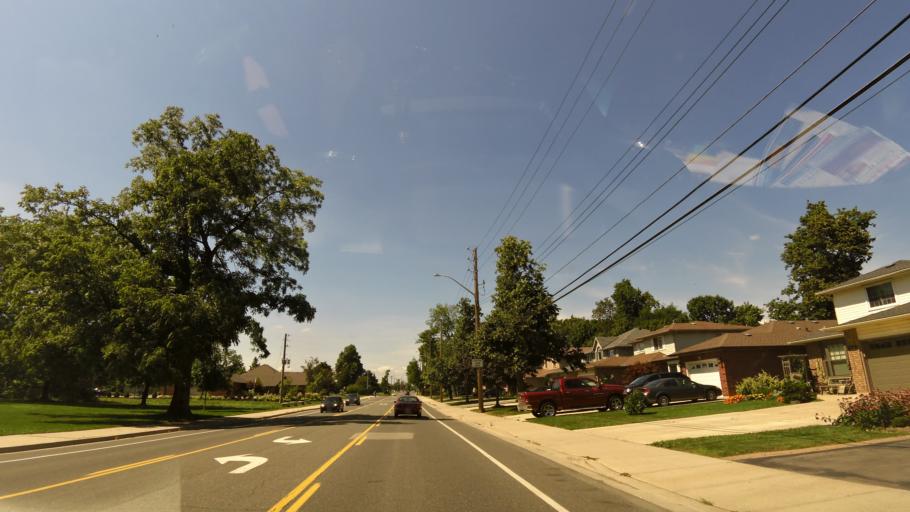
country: CA
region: Ontario
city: Hamilton
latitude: 43.2139
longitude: -79.9005
